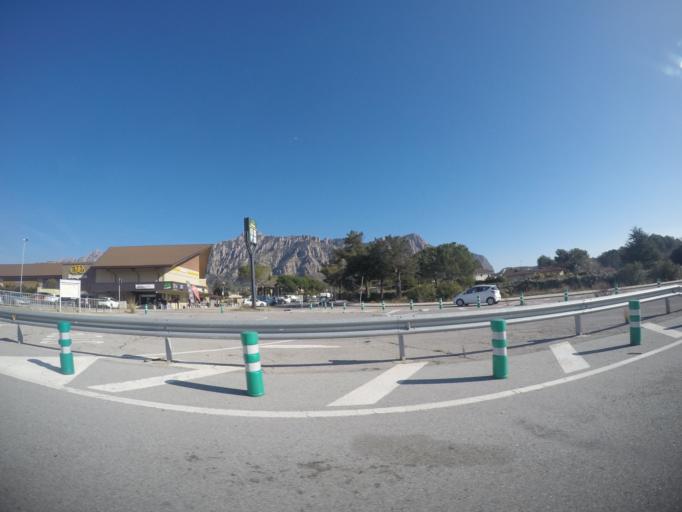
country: ES
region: Catalonia
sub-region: Provincia de Barcelona
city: Collbato
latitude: 41.5623
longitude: 1.8167
